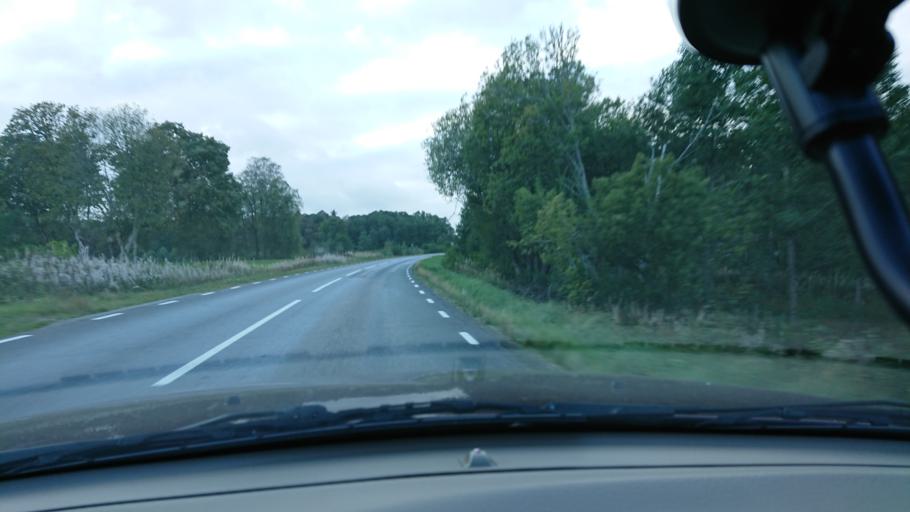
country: SE
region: Kronoberg
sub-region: Vaxjo Kommun
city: Lammhult
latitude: 57.0683
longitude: 14.7262
